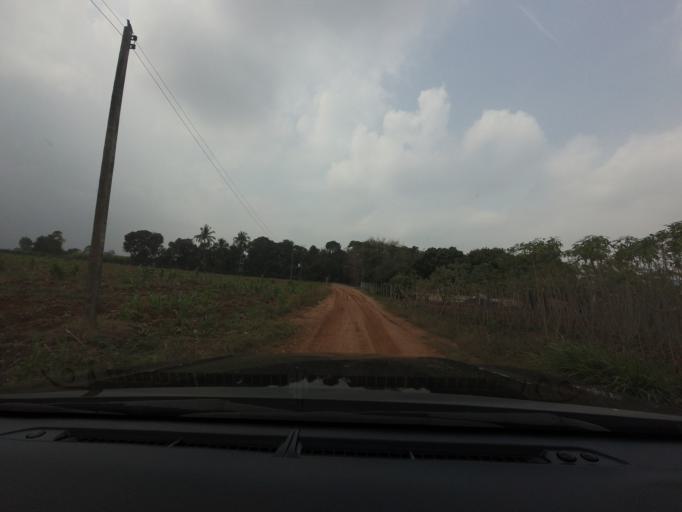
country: TH
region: Nakhon Ratchasima
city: Wang Nam Khiao
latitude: 14.4781
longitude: 101.6419
